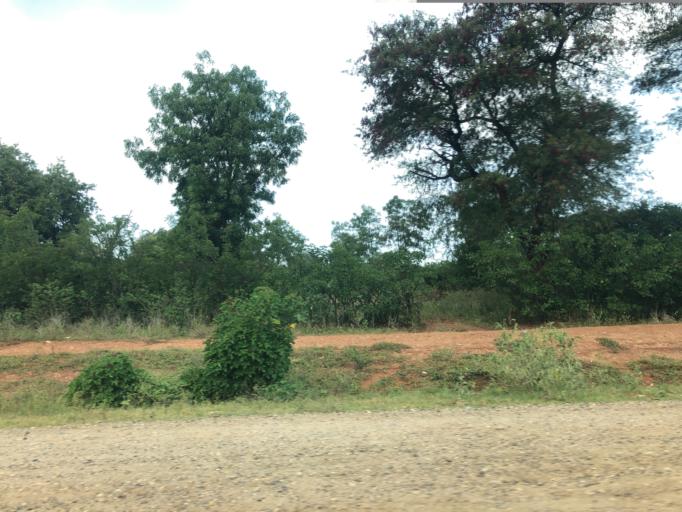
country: ET
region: Southern Nations, Nationalities, and People's Region
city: Turmi
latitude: 5.1706
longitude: 36.5454
